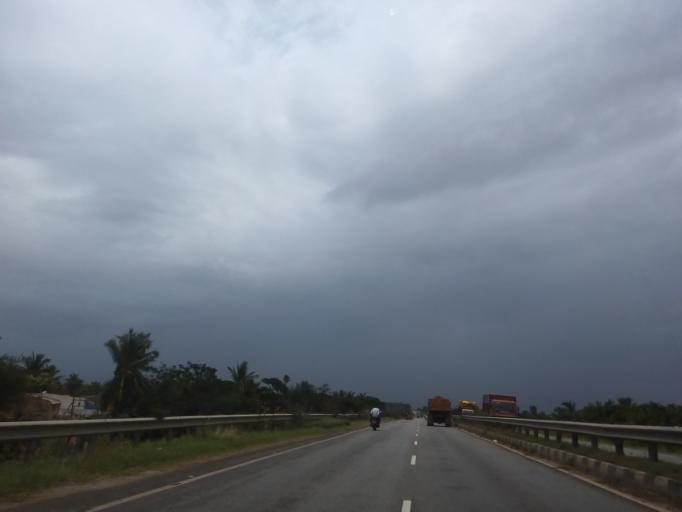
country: IN
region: Karnataka
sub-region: Davanagere
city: Harihar
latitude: 14.4695
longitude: 75.8361
